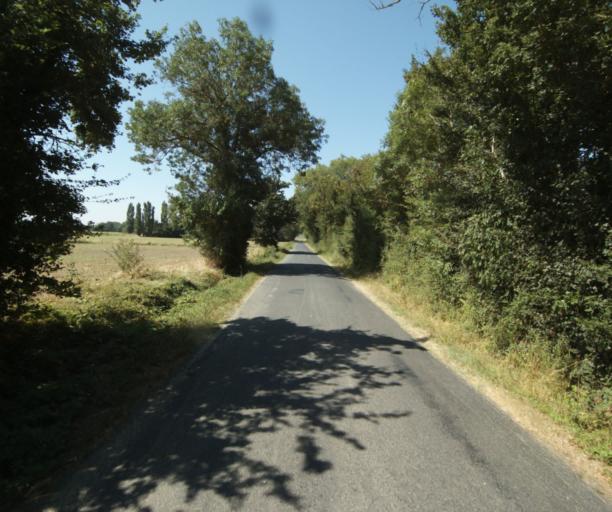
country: FR
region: Midi-Pyrenees
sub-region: Departement du Tarn
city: Puylaurens
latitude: 43.5195
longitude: 1.9634
